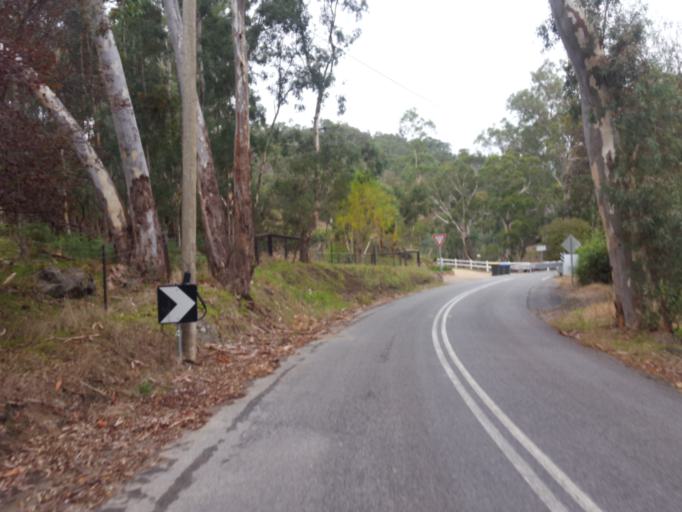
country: AU
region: South Australia
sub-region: Campbelltown
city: Athelstone
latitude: -34.8770
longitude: 138.7562
